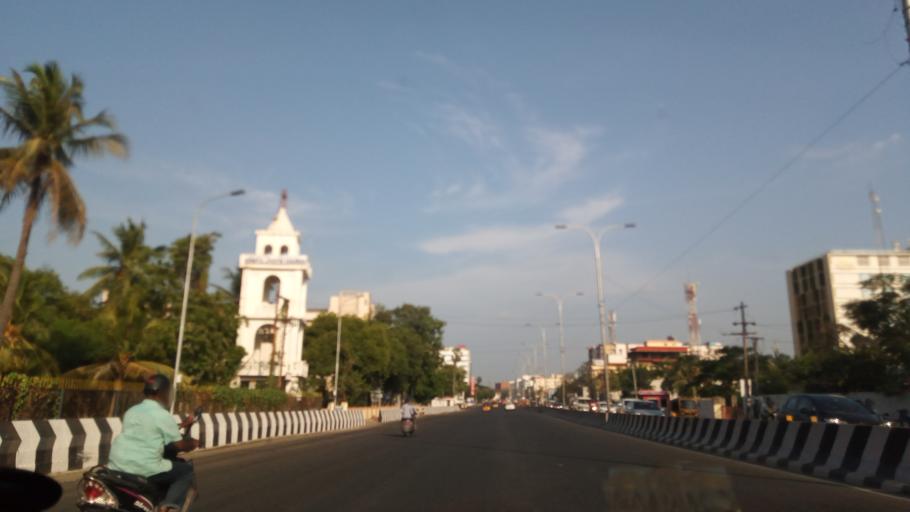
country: IN
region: Tamil Nadu
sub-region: Kancheepuram
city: Manappakkam
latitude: 13.0232
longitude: 80.1799
